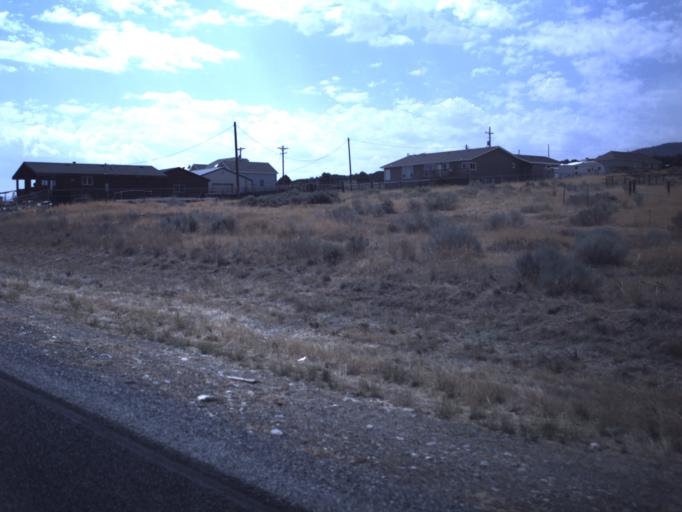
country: US
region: Utah
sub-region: Utah County
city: Eagle Mountain
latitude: 40.3222
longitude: -112.1024
